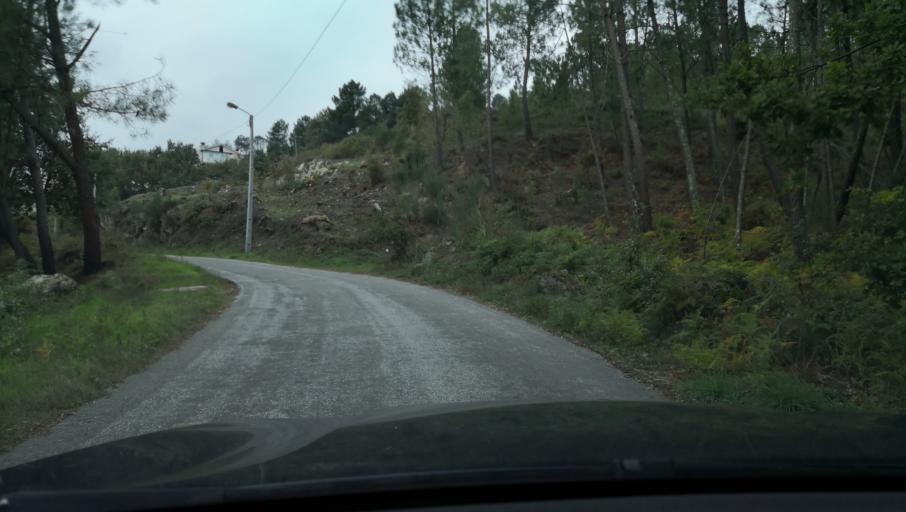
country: PT
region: Vila Real
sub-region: Vila Real
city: Vila Real
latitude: 41.3226
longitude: -7.7564
